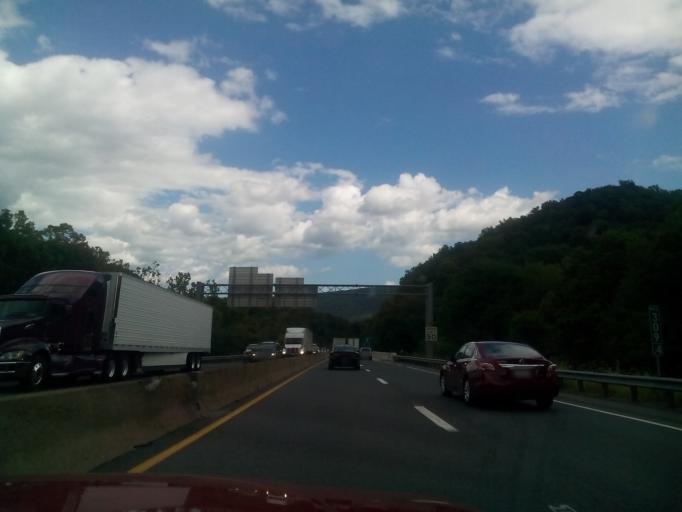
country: US
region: Pennsylvania
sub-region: Monroe County
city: East Stroudsburg
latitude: 40.9984
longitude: -75.1517
